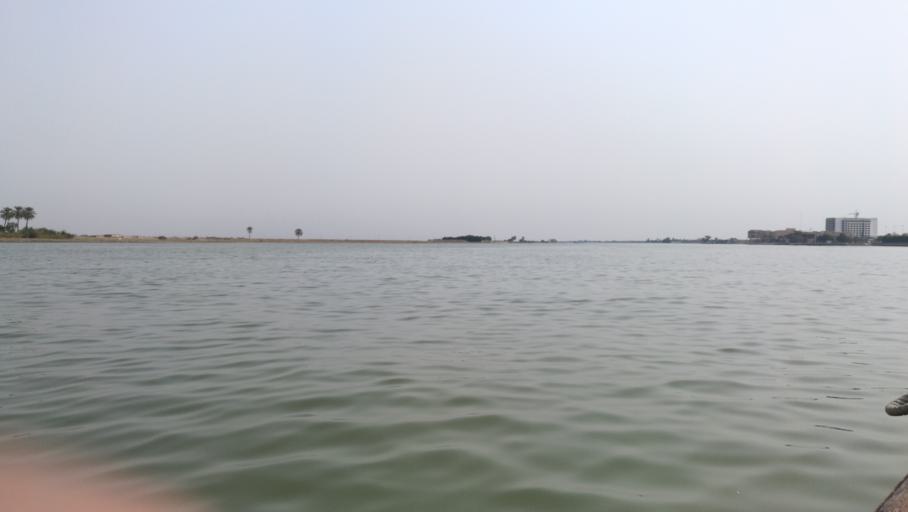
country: IQ
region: Basra Governorate
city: Al Basrah al Qadimah
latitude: 30.5036
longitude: 47.8579
